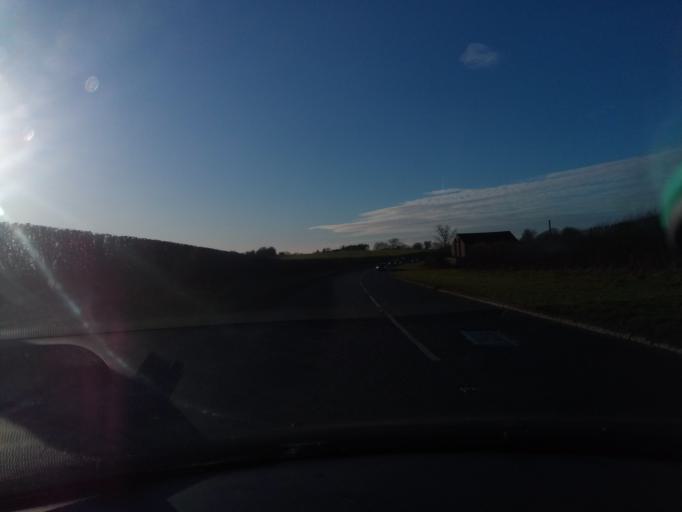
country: GB
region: England
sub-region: North Yorkshire
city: Thirsk
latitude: 54.2136
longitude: -1.4292
